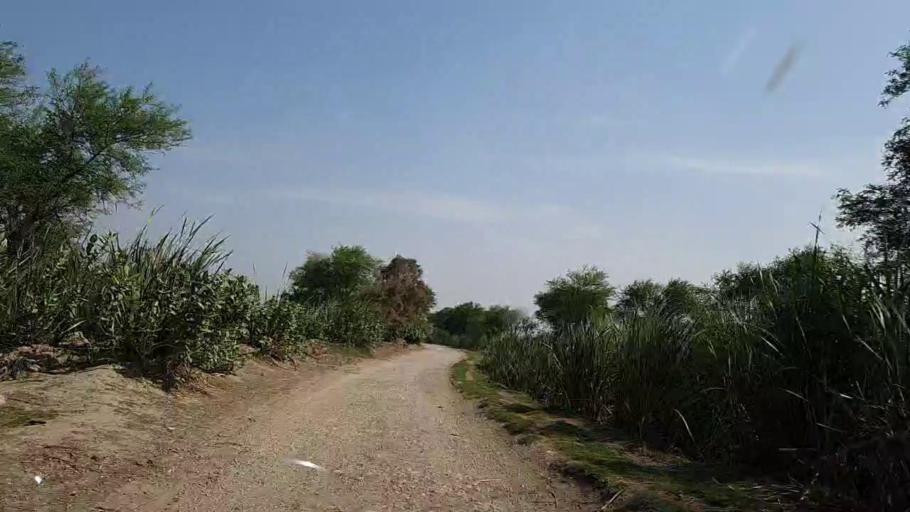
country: PK
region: Sindh
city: Khanpur
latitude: 27.7236
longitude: 69.3604
